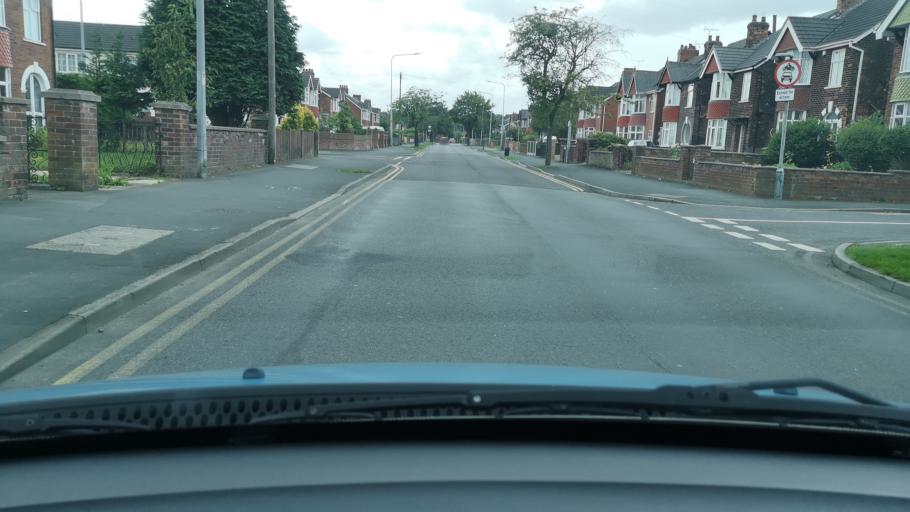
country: GB
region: England
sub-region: North Lincolnshire
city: Scunthorpe
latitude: 53.5899
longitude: -0.6610
